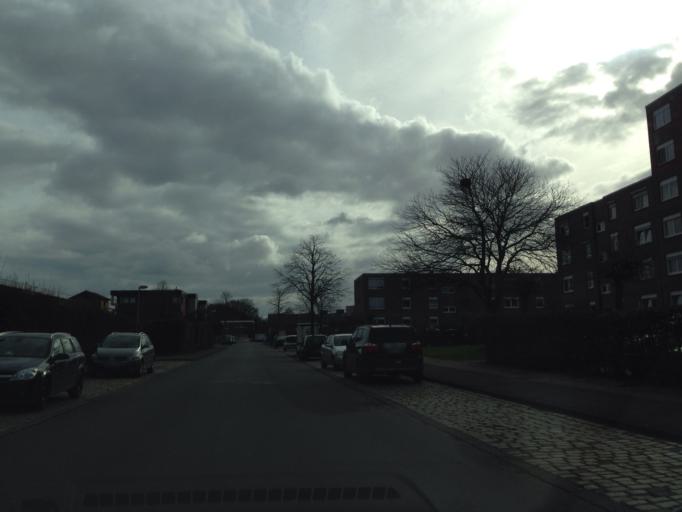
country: DE
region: North Rhine-Westphalia
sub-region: Regierungsbezirk Munster
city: Muenster
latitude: 52.0018
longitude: 7.5993
